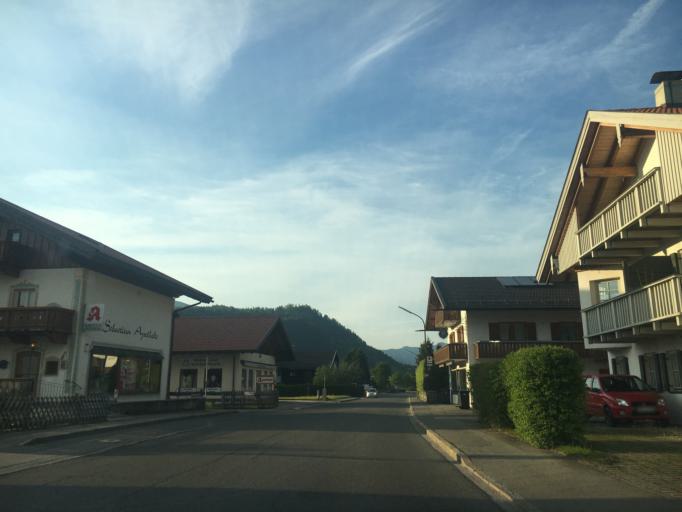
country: DE
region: Bavaria
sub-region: Upper Bavaria
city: Krun
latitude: 47.5063
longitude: 11.2783
